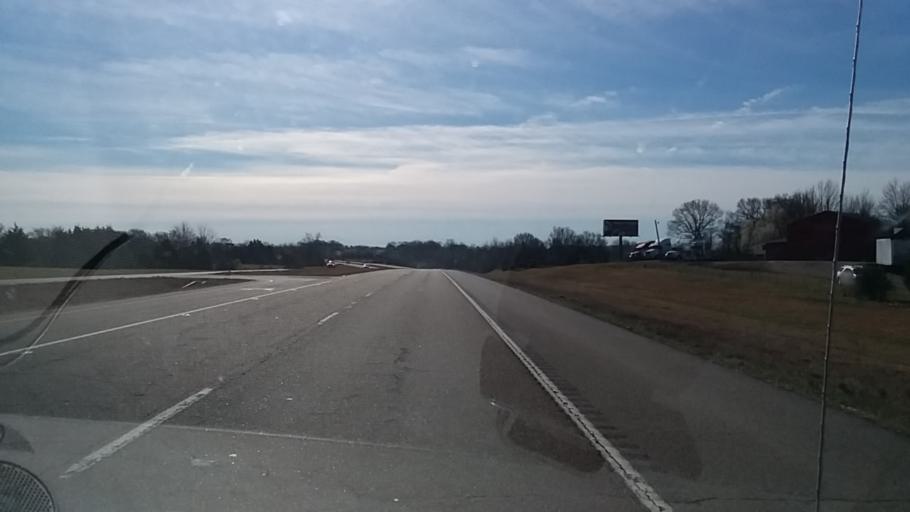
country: US
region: Tennessee
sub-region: Crockett County
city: Alamo
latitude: 35.7813
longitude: -89.1416
